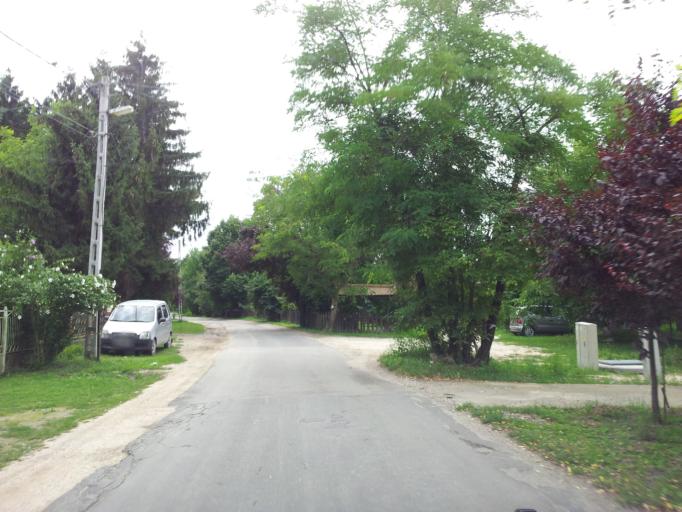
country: HU
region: Pest
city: Rackeve
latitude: 47.2021
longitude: 18.9602
